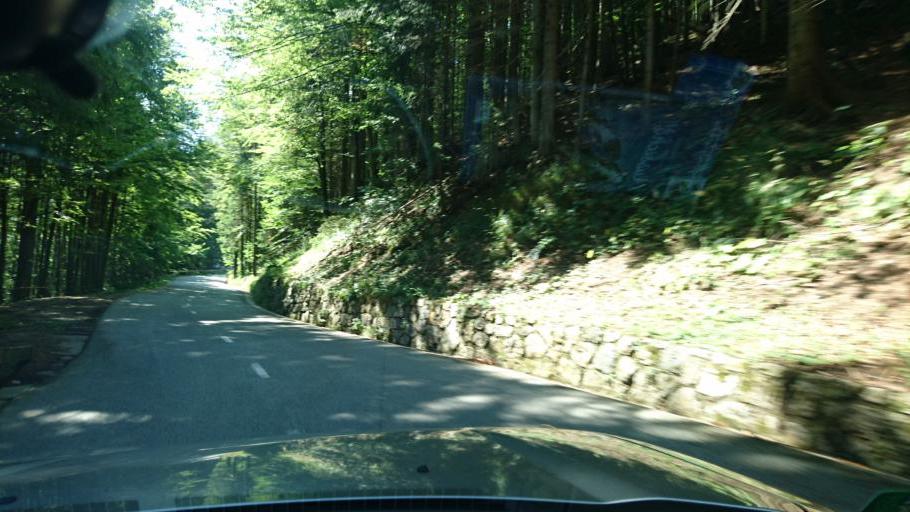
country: SI
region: Kranjska Gora
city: Kranjska Gora
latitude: 46.4564
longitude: 13.7802
